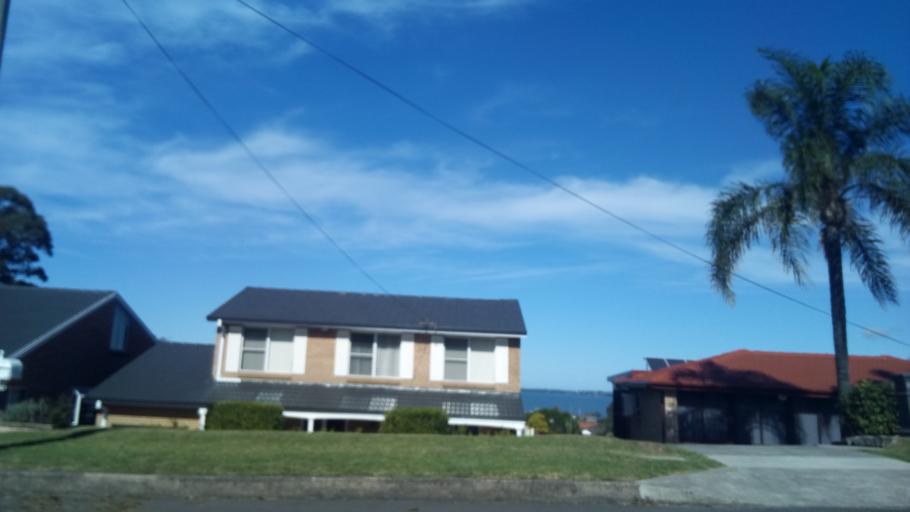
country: AU
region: New South Wales
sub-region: Wollongong
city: Koonawarra
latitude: -34.4953
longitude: 150.8142
